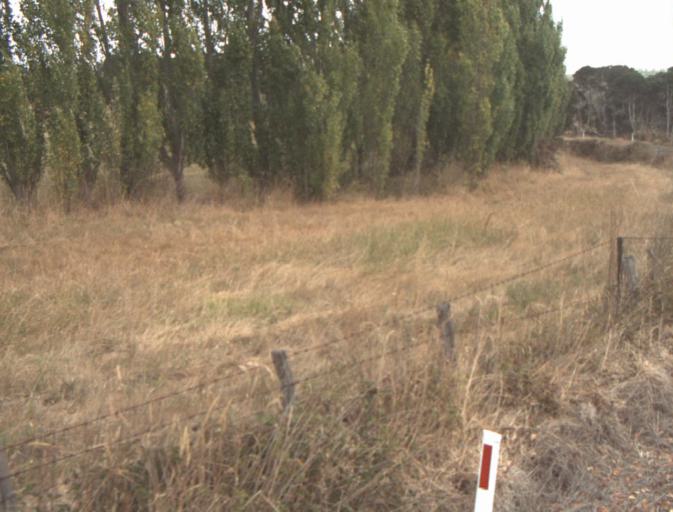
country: AU
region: Tasmania
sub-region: Launceston
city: Mayfield
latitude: -41.2892
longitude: 146.9915
